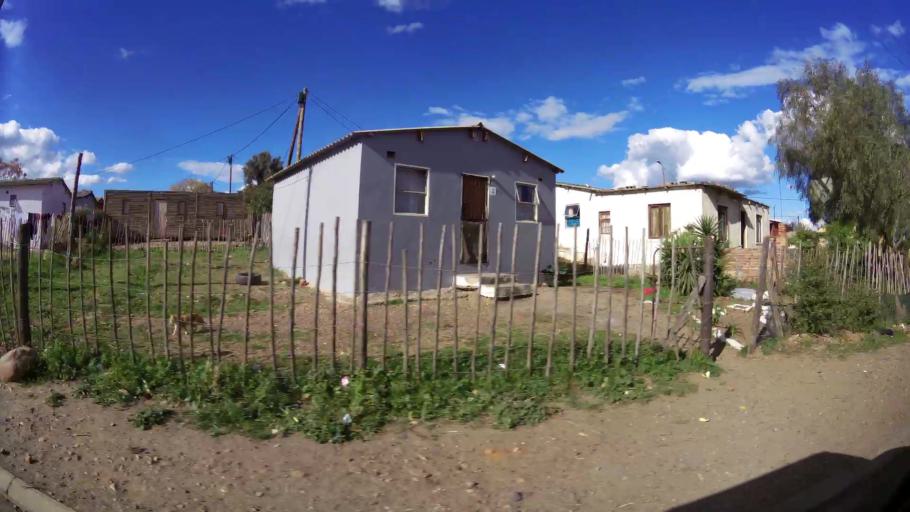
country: ZA
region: Western Cape
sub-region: Overberg District Municipality
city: Swellendam
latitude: -34.0442
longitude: 20.4452
